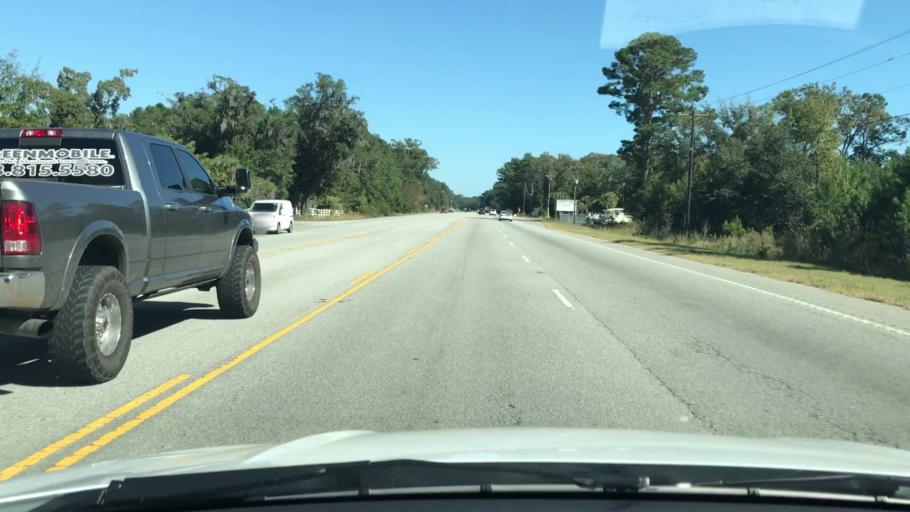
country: US
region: South Carolina
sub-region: Beaufort County
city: Bluffton
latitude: 32.3548
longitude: -80.8870
